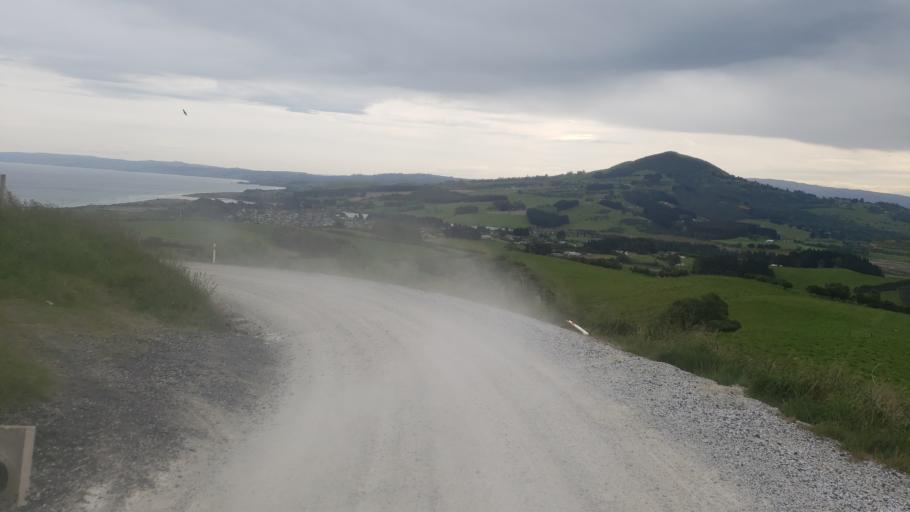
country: NZ
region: Otago
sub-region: Dunedin City
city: Dunedin
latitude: -45.9170
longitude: 170.4281
